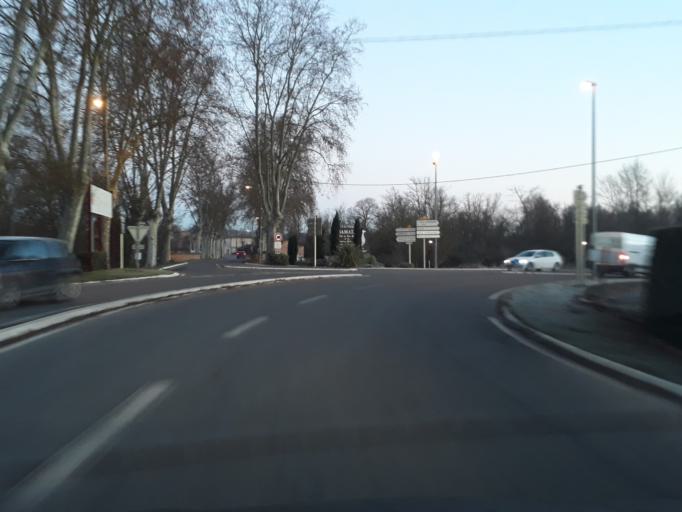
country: FR
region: Midi-Pyrenees
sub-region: Departement du Gers
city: Samatan
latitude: 43.4870
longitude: 0.9345
